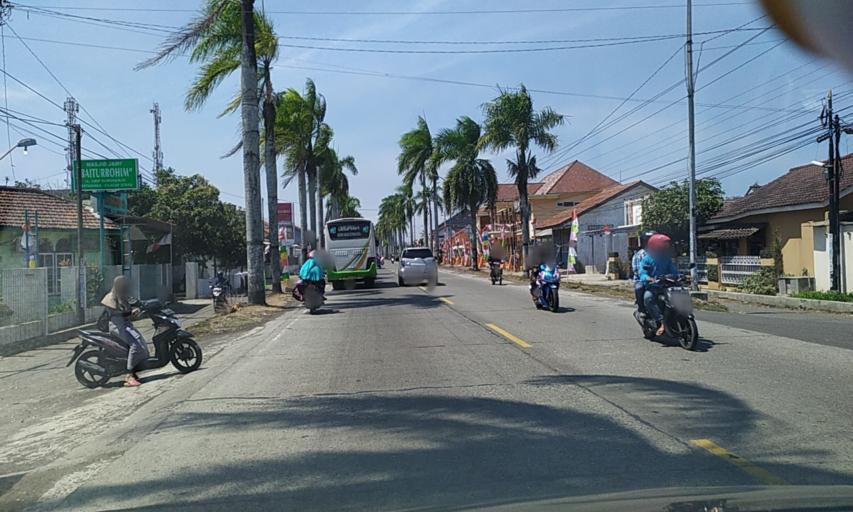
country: ID
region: Central Java
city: Rejanegara
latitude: -7.6786
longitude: 109.0547
